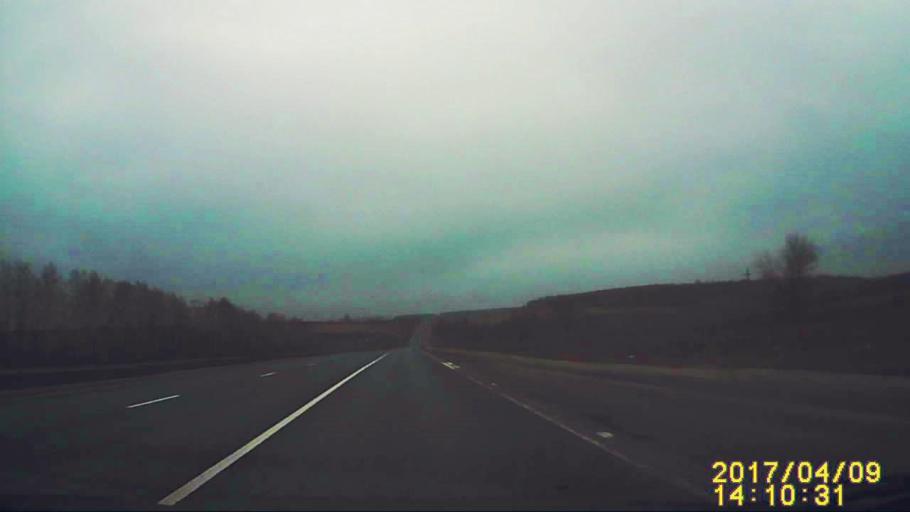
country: RU
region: Ulyanovsk
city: Krasnyy Gulyay
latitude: 54.0392
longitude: 48.2135
